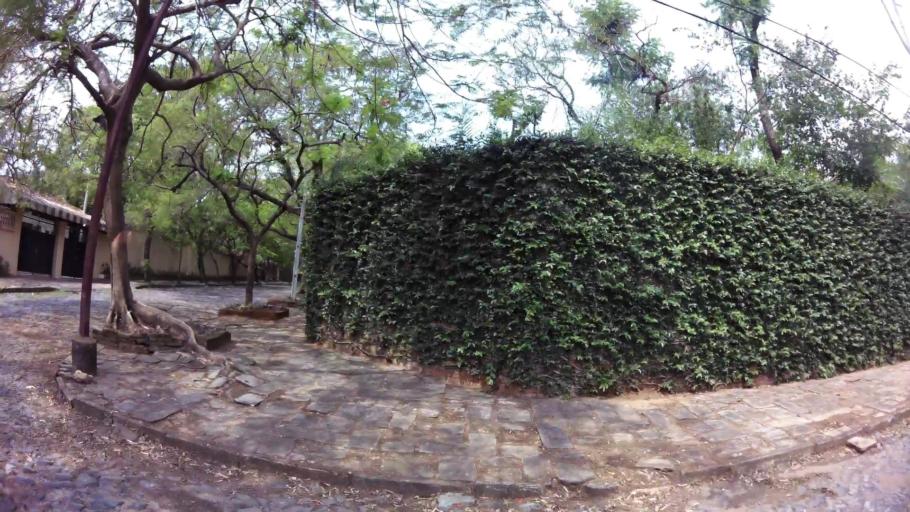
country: PY
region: Asuncion
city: Asuncion
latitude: -25.2863
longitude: -57.5824
